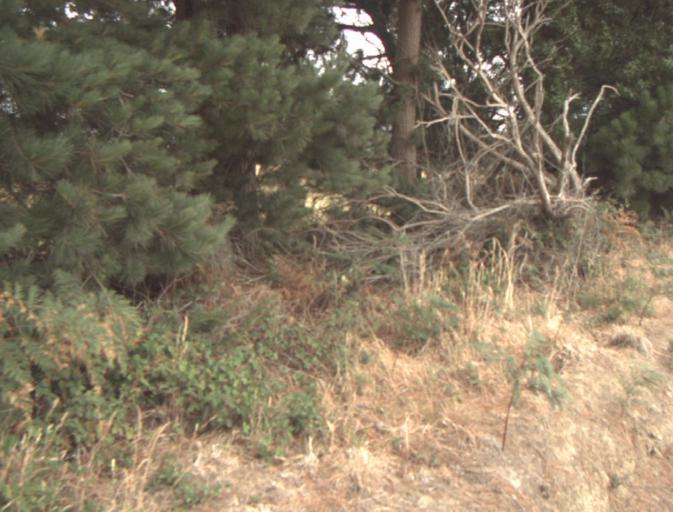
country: AU
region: Tasmania
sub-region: Launceston
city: Mayfield
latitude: -41.1719
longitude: 147.2127
